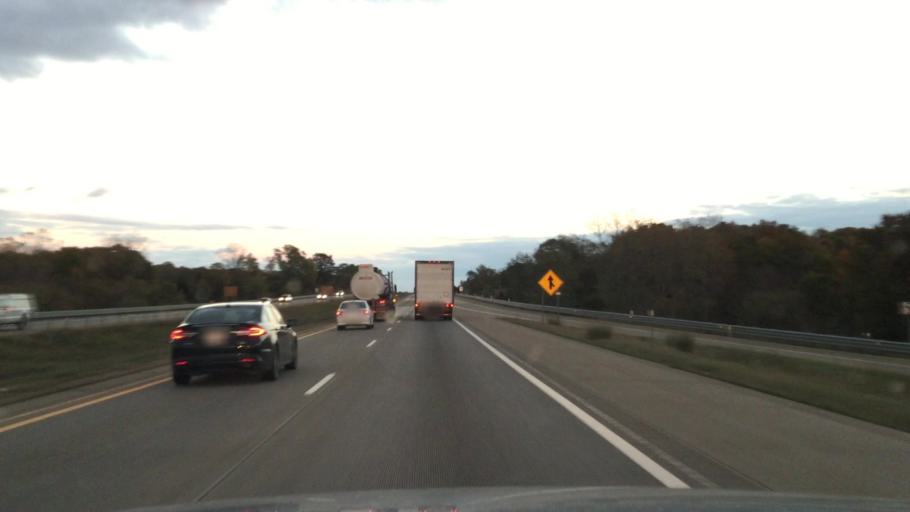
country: US
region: Michigan
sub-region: Jackson County
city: Grass Lake
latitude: 42.2918
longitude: -84.2517
